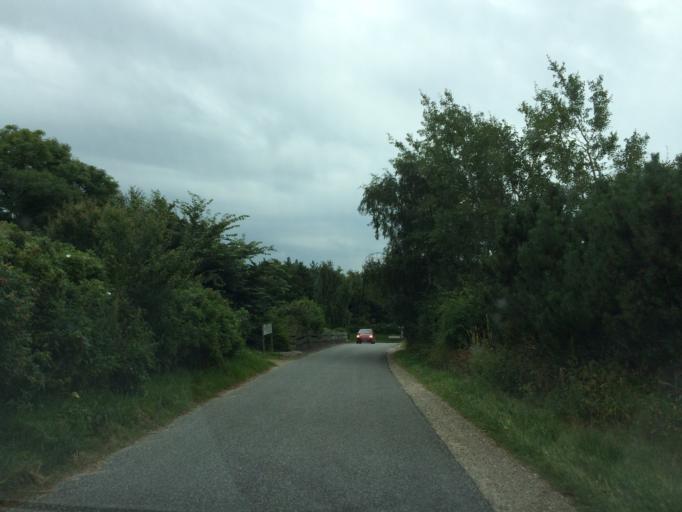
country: DK
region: Central Jutland
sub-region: Syddjurs Kommune
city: Ronde
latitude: 56.2411
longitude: 10.5546
